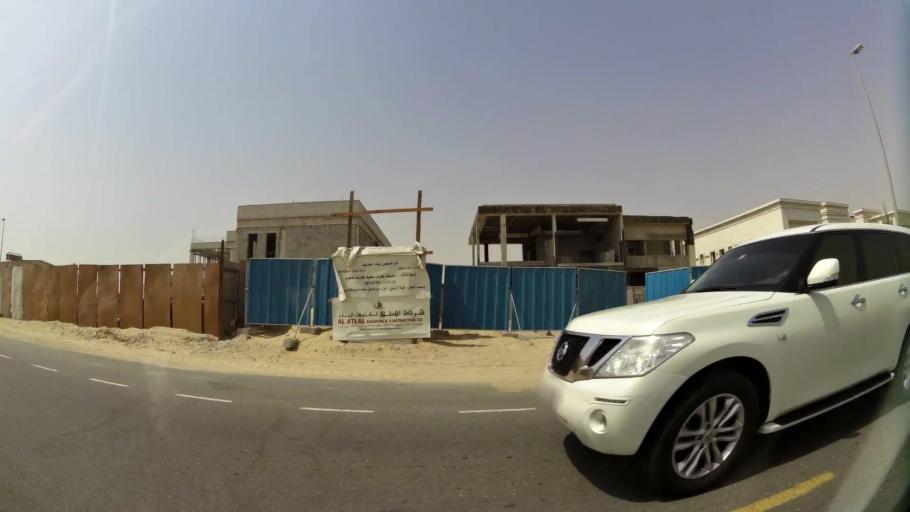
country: AE
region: Ash Shariqah
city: Sharjah
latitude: 25.2517
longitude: 55.4867
